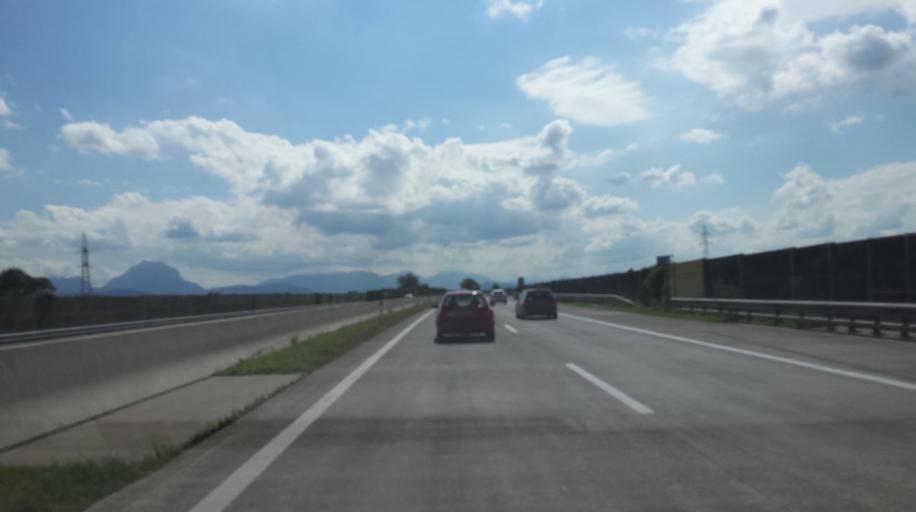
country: AT
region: Upper Austria
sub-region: Politischer Bezirk Gmunden
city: Vorchdorf
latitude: 48.0256
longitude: 13.9673
